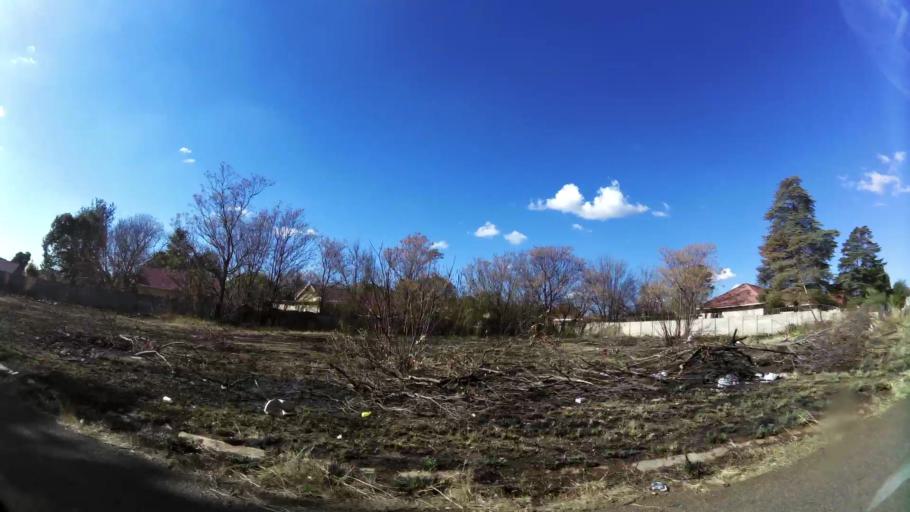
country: ZA
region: Gauteng
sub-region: West Rand District Municipality
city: Carletonville
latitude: -26.3741
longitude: 27.3986
